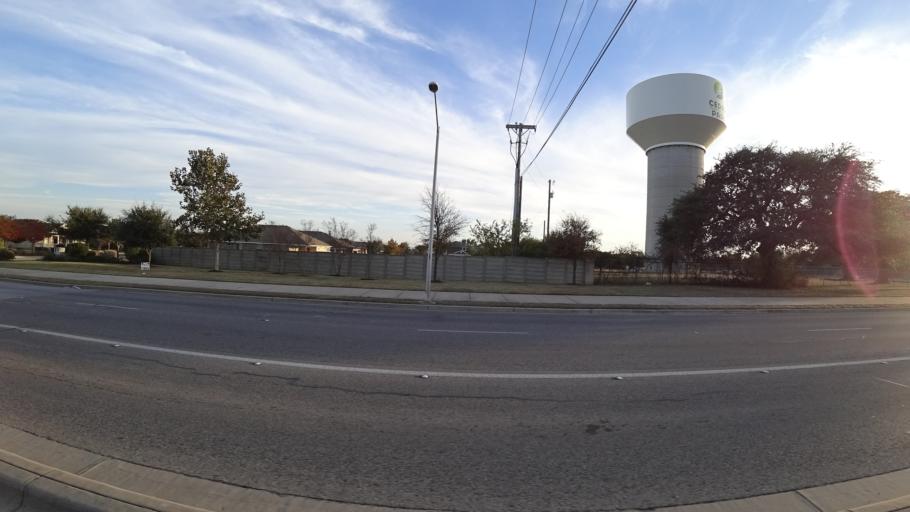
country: US
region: Texas
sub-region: Williamson County
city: Cedar Park
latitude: 30.5342
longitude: -97.8306
